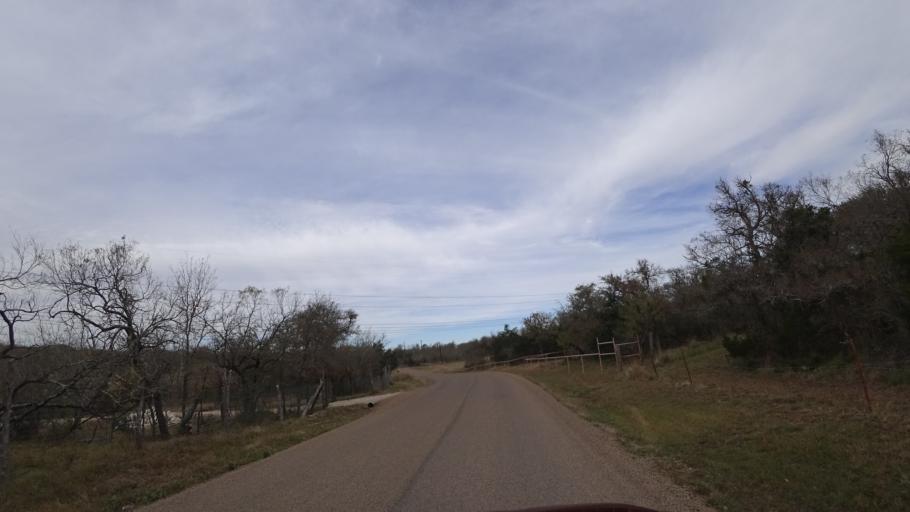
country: US
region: Texas
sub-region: Travis County
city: Garfield
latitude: 30.1102
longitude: -97.5630
